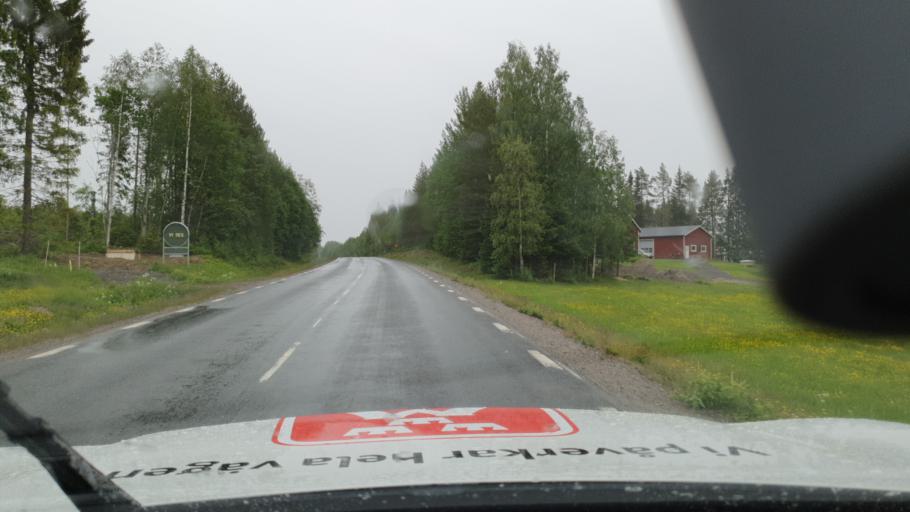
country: SE
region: Vaesterbotten
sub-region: Vannas Kommun
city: Vaennaes
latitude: 63.7724
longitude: 19.6862
